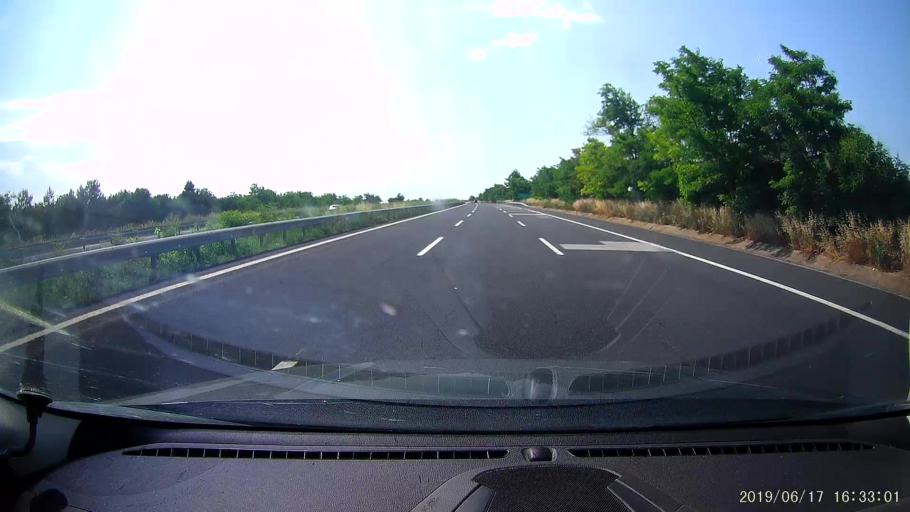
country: TR
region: Kirklareli
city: Buyukkaristiran
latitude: 41.3769
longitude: 27.5855
